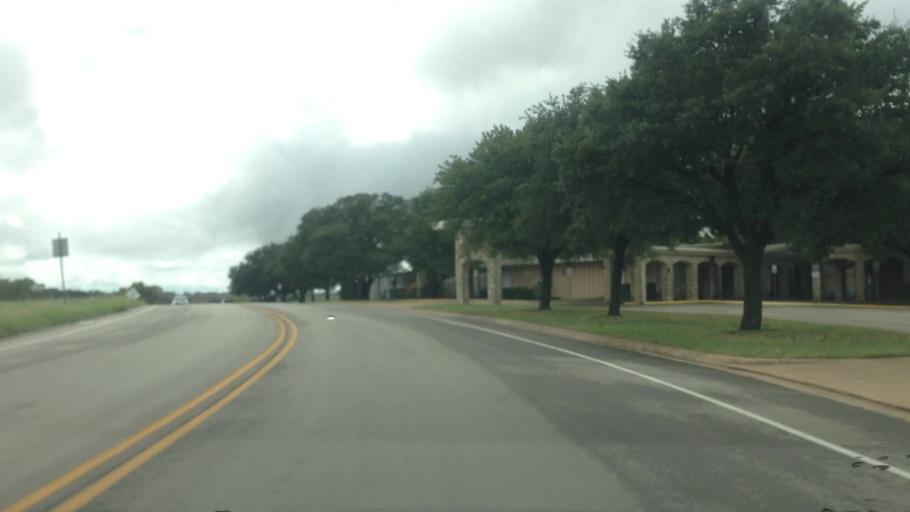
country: US
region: Texas
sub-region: Tarrant County
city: White Settlement
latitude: 32.7448
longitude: -97.4611
